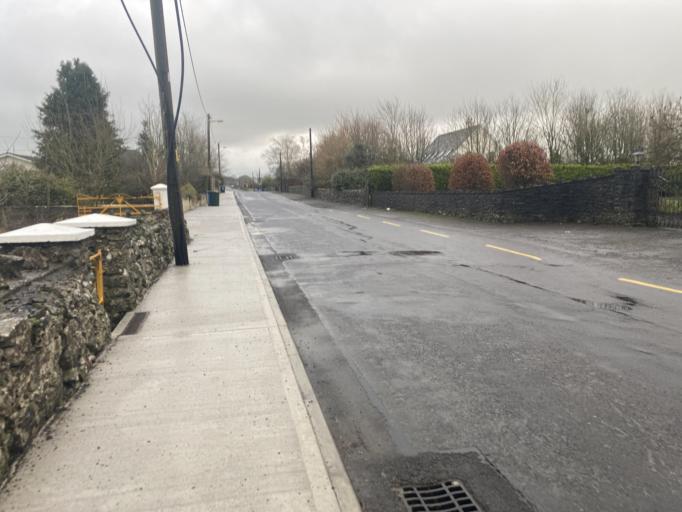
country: IE
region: Connaught
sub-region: County Galway
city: Tuam
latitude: 53.5209
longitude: -8.8311
